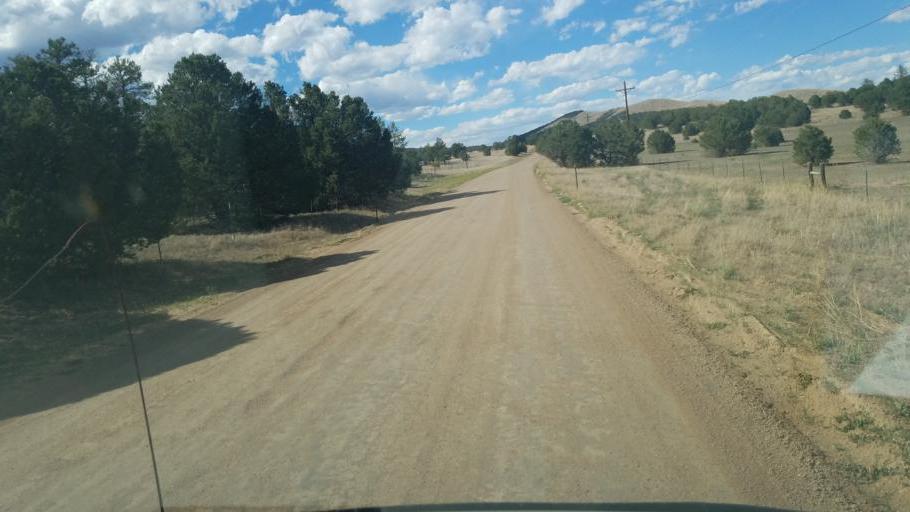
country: US
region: Colorado
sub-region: Custer County
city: Westcliffe
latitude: 38.3022
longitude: -105.4865
